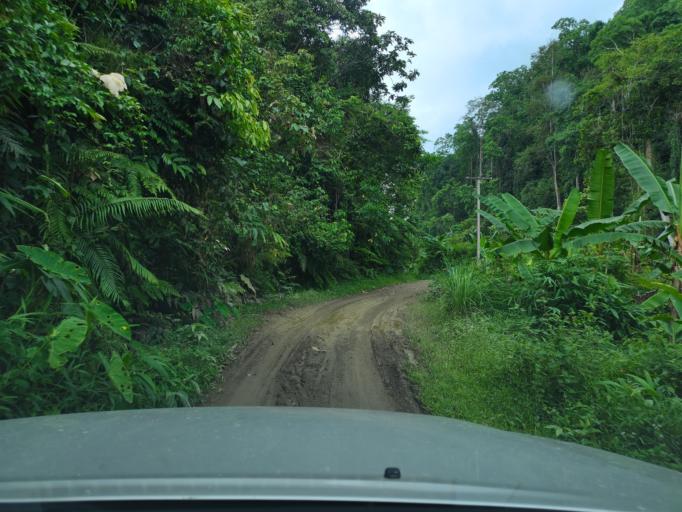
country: LA
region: Loungnamtha
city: Muang Long
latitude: 20.7773
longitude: 101.0168
